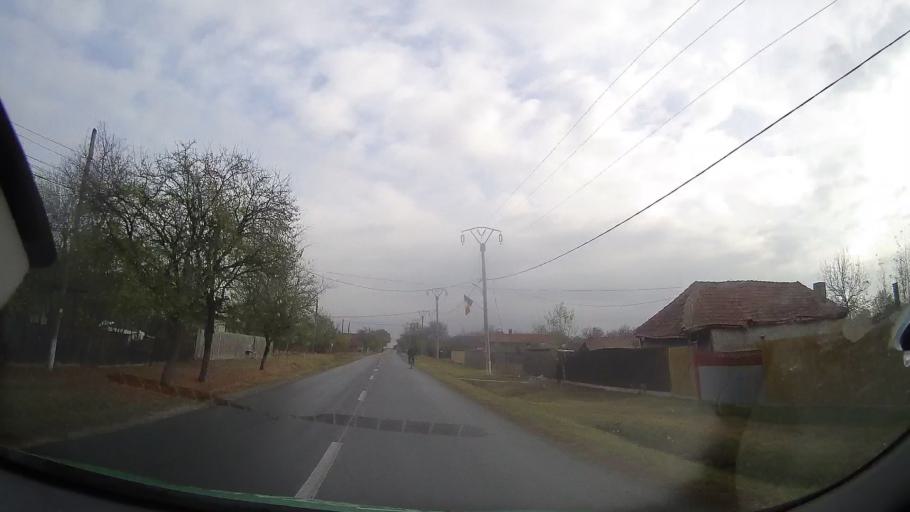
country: RO
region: Ialomita
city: Brazii
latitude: 44.7589
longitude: 26.3662
